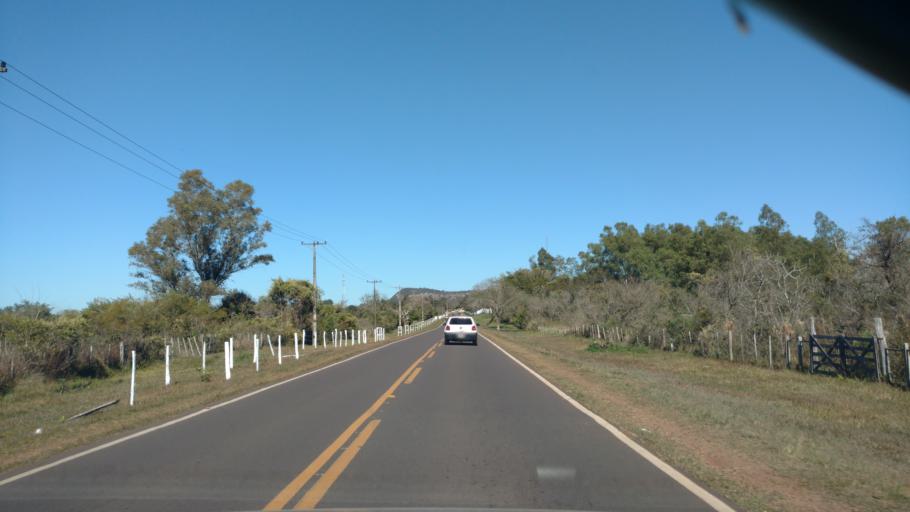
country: PY
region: Paraguari
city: Yaguaron
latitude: -25.5471
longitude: -57.2799
